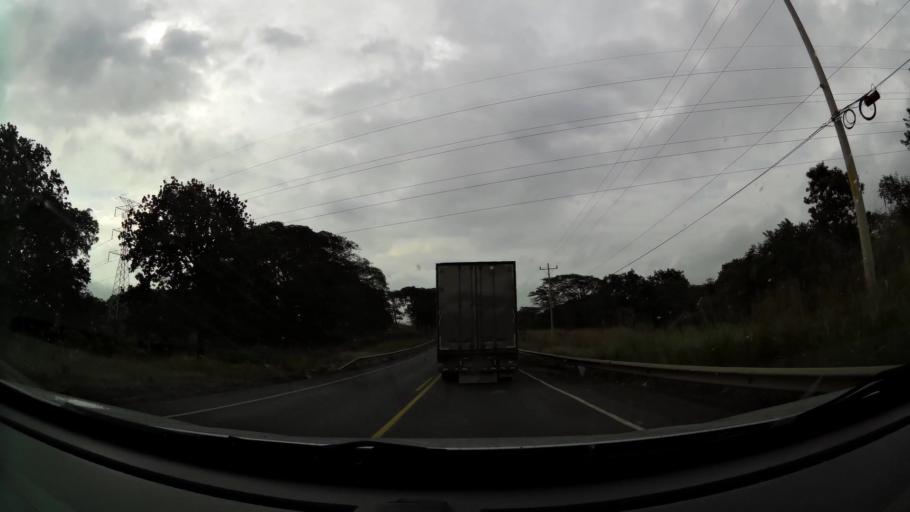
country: CR
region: Alajuela
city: Carrillos
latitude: 9.9686
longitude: -84.2805
